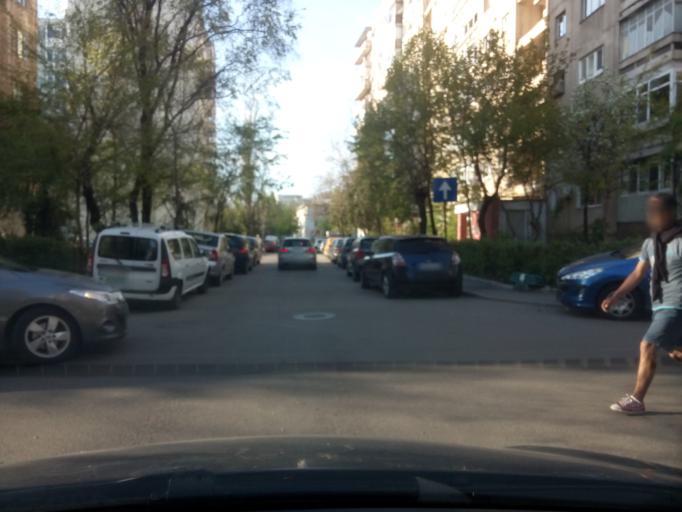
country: RO
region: Ilfov
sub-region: Comuna Fundeni-Dobroesti
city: Fundeni
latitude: 44.4332
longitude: 26.1572
